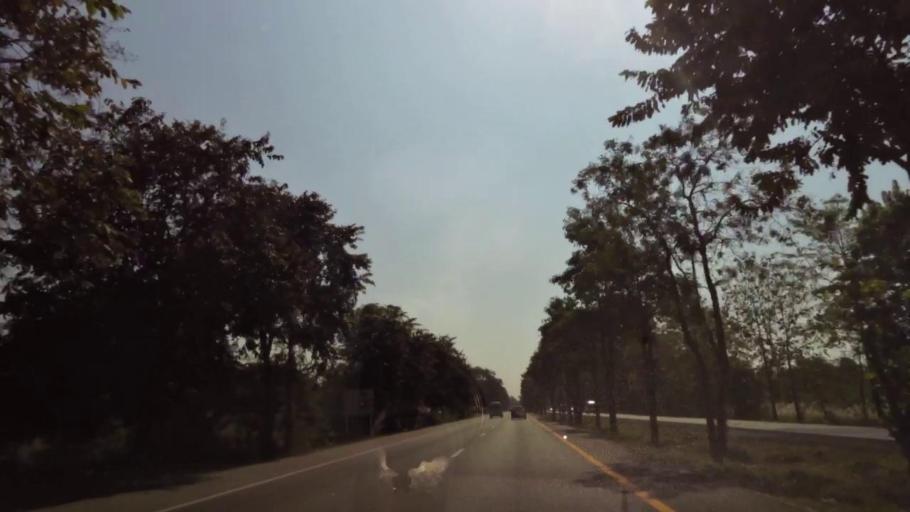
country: TH
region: Phichit
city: Bueng Na Rang
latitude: 16.0725
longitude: 100.1240
